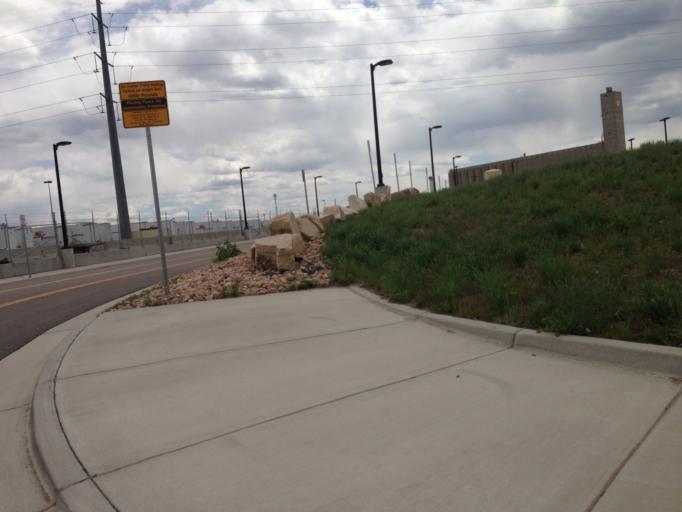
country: US
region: Colorado
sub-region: Adams County
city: Twin Lakes
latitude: 39.8070
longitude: -105.0035
